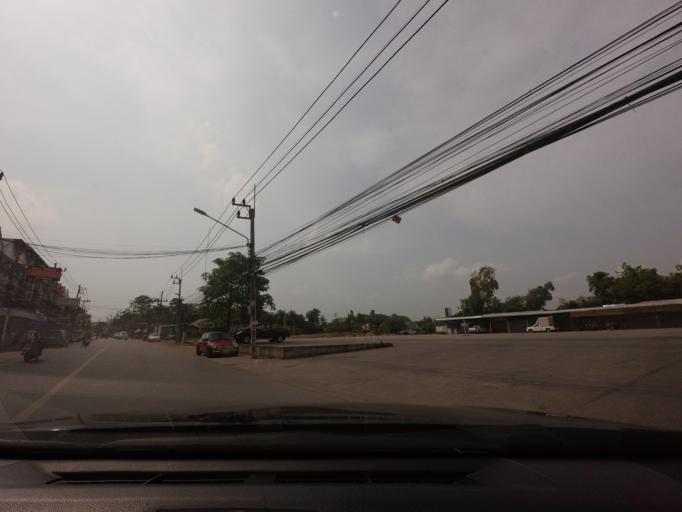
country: TH
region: Surat Thani
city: Surat Thani
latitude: 9.1069
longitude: 99.3084
